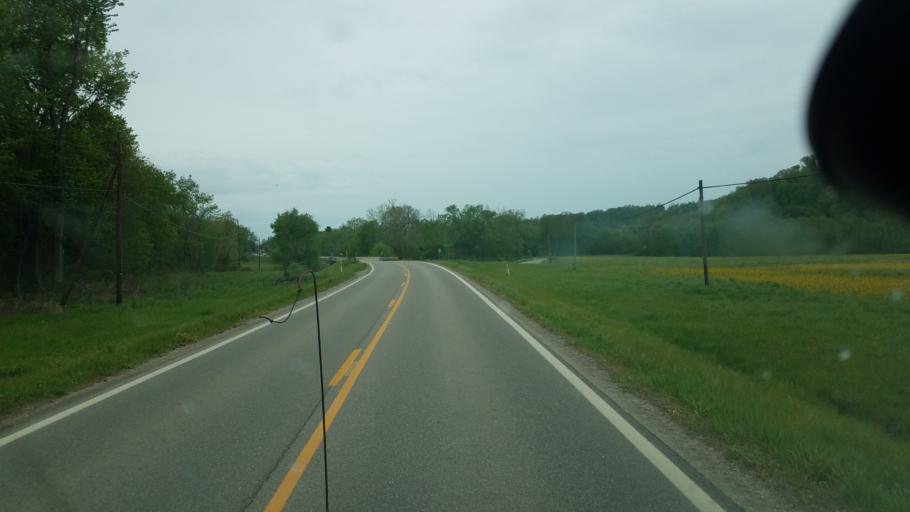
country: US
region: Ohio
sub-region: Guernsey County
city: Cambridge
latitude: 40.1508
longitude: -81.5642
